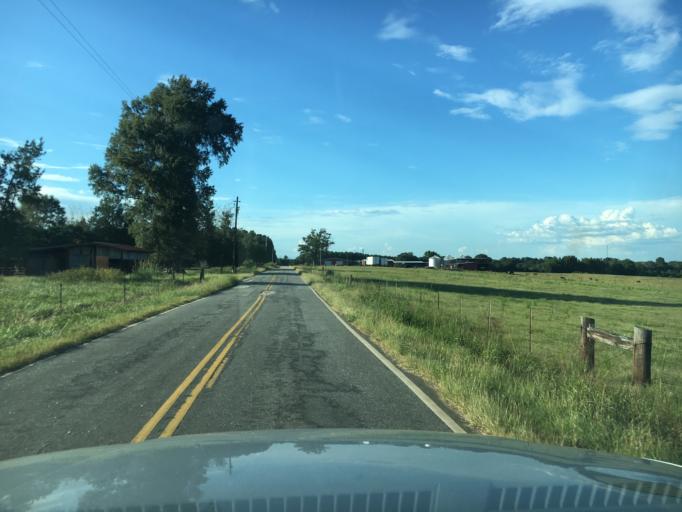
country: US
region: South Carolina
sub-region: Spartanburg County
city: Woodruff
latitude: 34.8248
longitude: -82.0998
